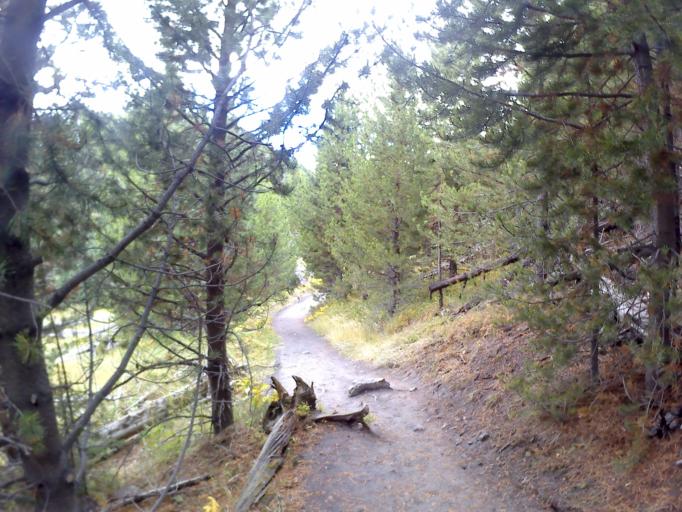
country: US
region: Montana
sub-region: Gallatin County
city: West Yellowstone
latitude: 44.4848
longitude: -110.8665
